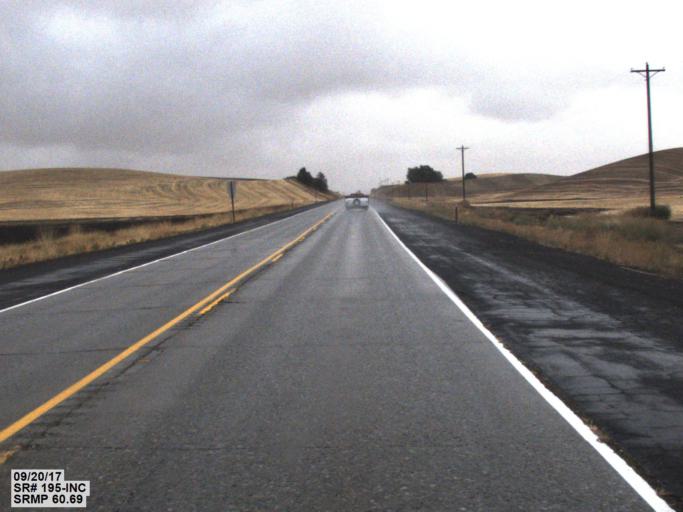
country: US
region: Washington
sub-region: Whitman County
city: Colfax
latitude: 47.1843
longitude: -117.3756
